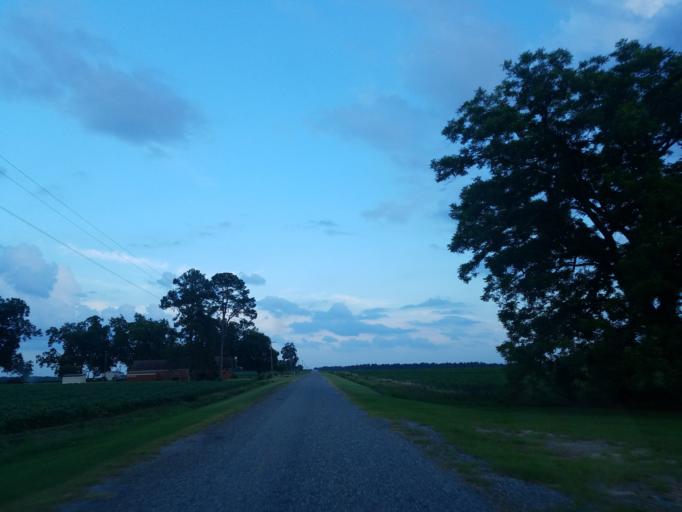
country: US
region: Georgia
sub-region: Dooly County
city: Vienna
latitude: 32.1635
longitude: -83.7316
